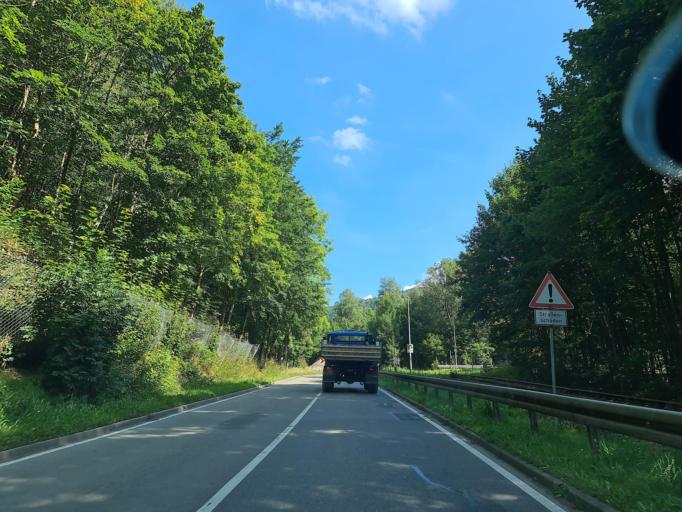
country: DE
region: Saxony
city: Heidersdorf
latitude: 50.6466
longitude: 13.3931
